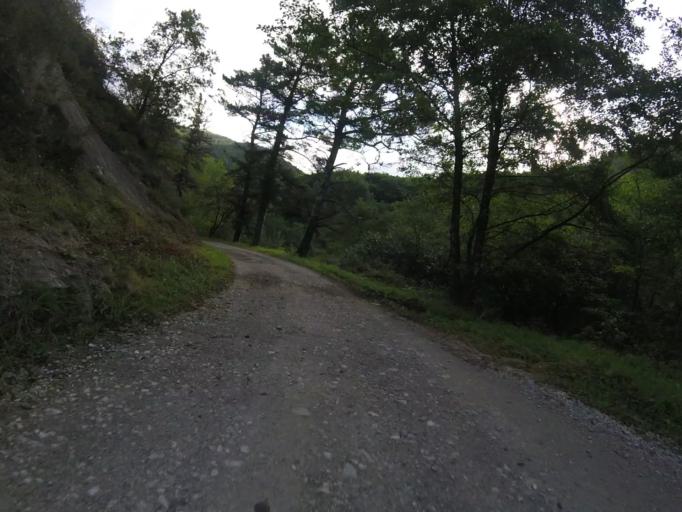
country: ES
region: Basque Country
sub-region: Provincia de Guipuzcoa
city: Elduayen
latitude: 43.1736
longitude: -1.9840
